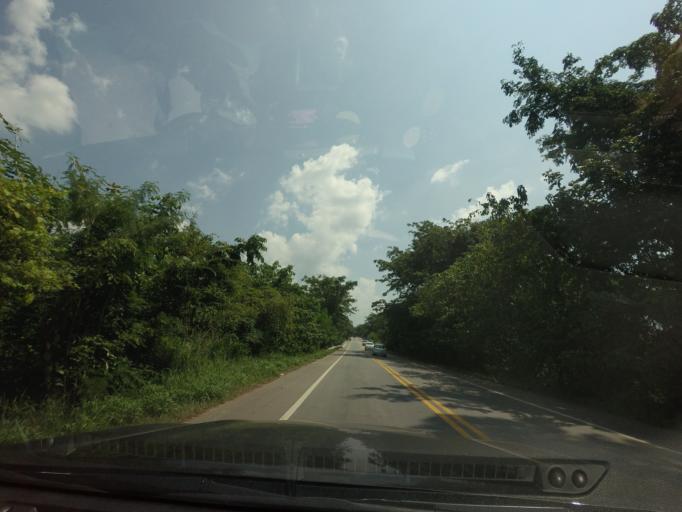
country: TH
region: Uttaradit
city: Thong Saen Khan
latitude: 17.3005
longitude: 100.4048
